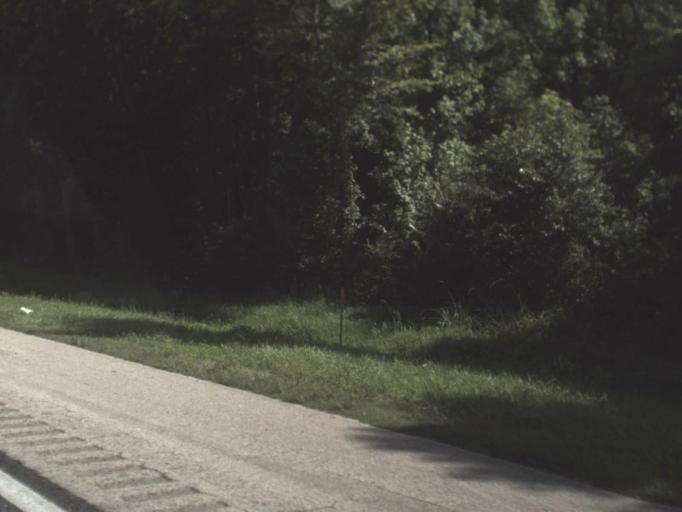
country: US
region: Florida
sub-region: Alachua County
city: Gainesville
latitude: 29.5517
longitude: -82.3392
